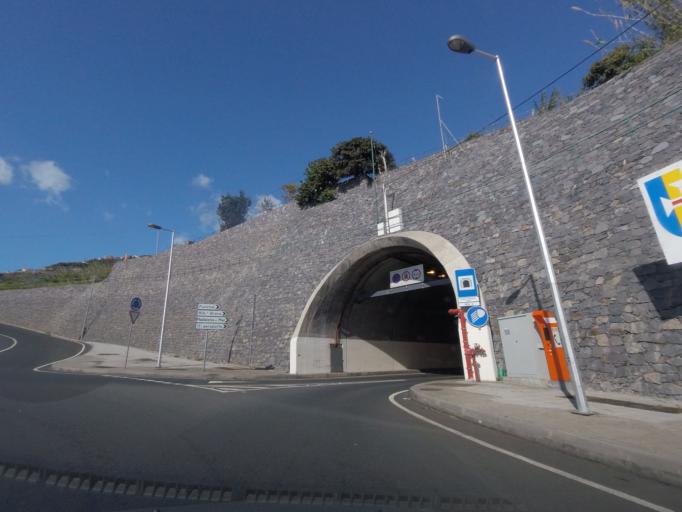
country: PT
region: Madeira
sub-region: Calheta
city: Arco da Calheta
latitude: 32.7115
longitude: -17.1522
